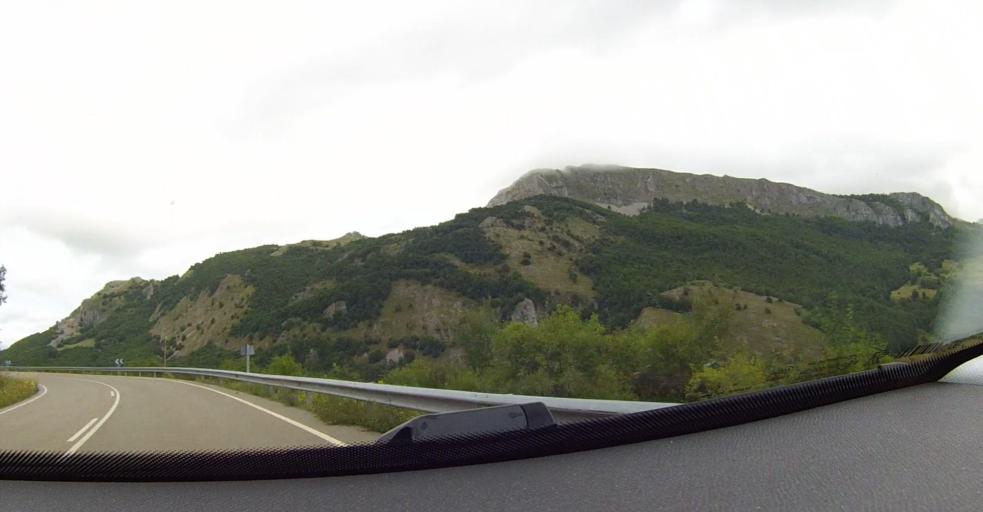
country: ES
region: Castille and Leon
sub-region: Provincia de Leon
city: Buron
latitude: 43.0162
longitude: -5.0330
